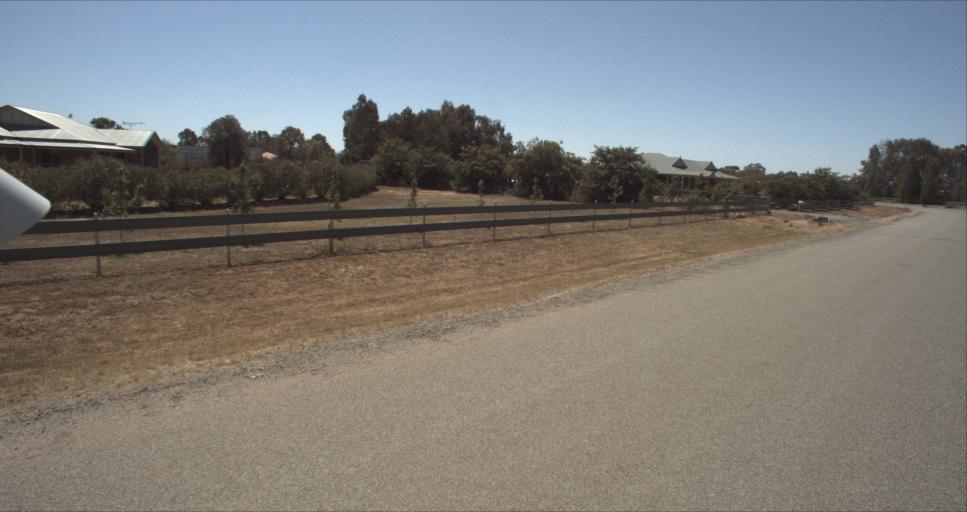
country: AU
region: New South Wales
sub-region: Leeton
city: Leeton
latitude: -34.5301
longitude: 146.3972
